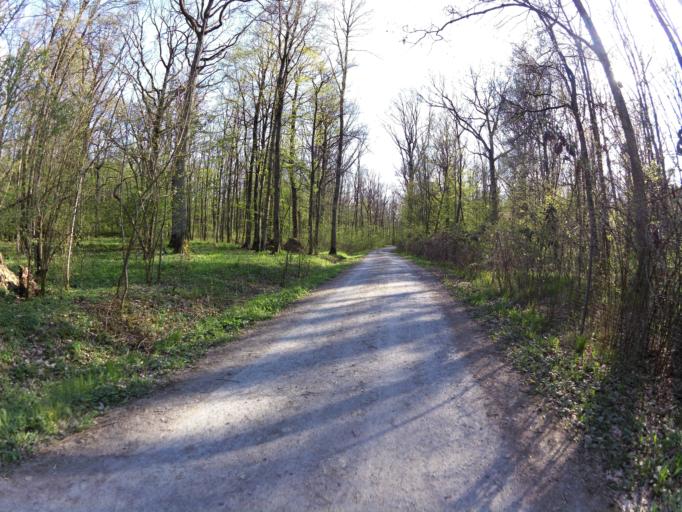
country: DE
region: Bavaria
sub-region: Regierungsbezirk Unterfranken
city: Rimpar
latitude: 49.8685
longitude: 9.9952
